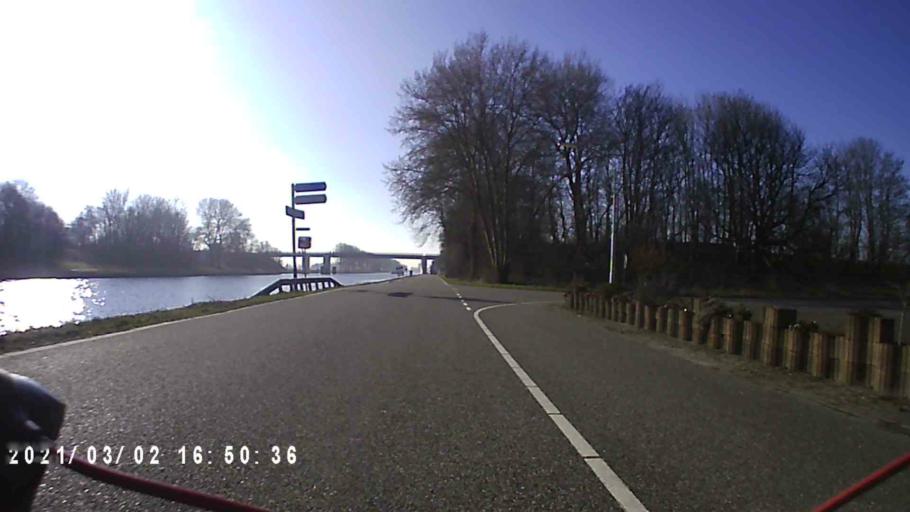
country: NL
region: Groningen
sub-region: Gemeente Grootegast
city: Grootegast
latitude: 53.2429
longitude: 6.2533
